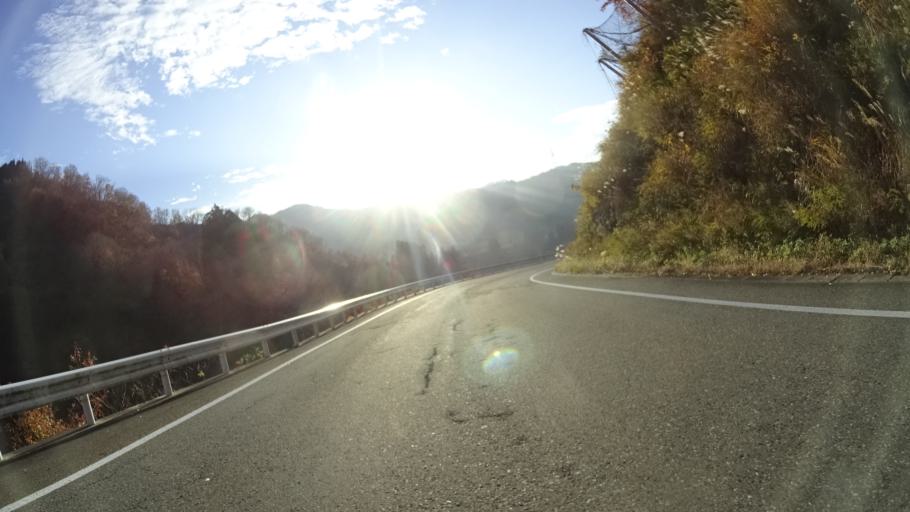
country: JP
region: Niigata
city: Shiozawa
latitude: 36.9843
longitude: 138.7533
